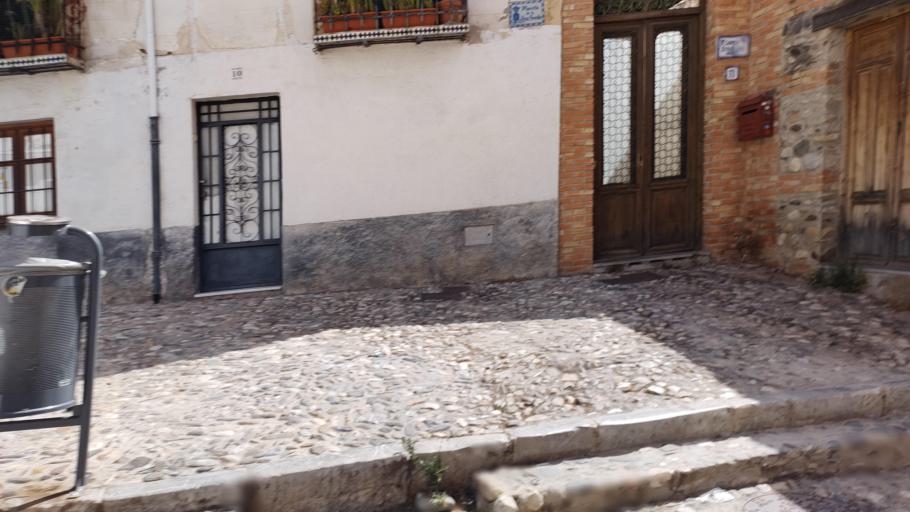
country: ES
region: Andalusia
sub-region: Provincia de Granada
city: Granada
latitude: 37.1791
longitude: -3.5949
